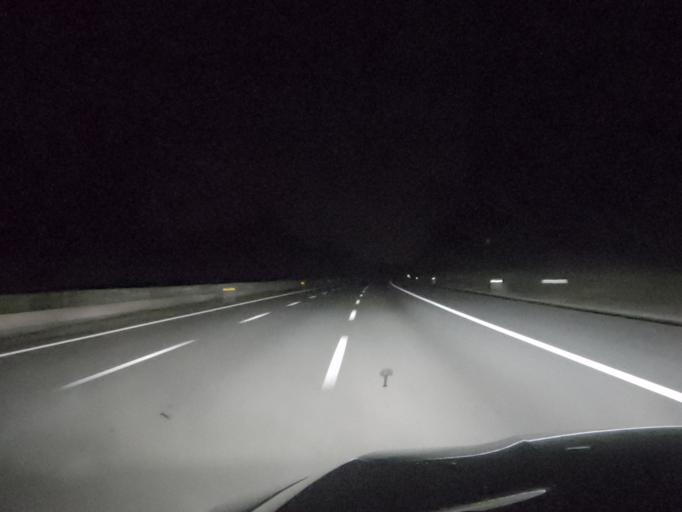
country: PT
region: Aveiro
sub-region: Ovar
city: Valega
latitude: 40.8312
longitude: -8.5545
